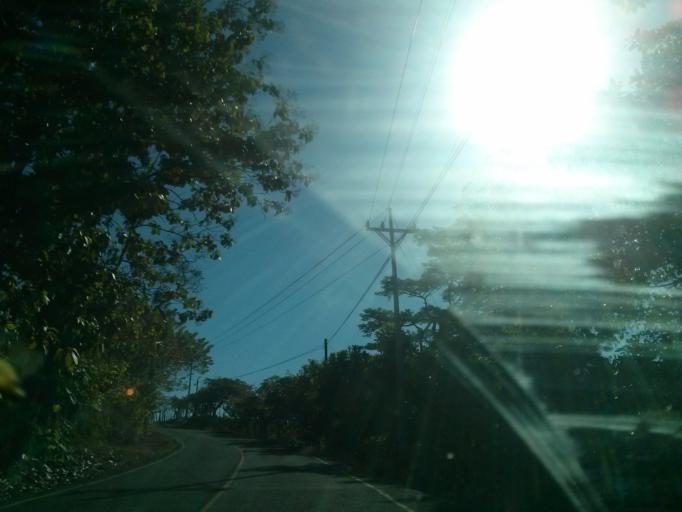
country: CR
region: Puntarenas
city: Paquera
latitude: 9.7026
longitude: -85.0422
